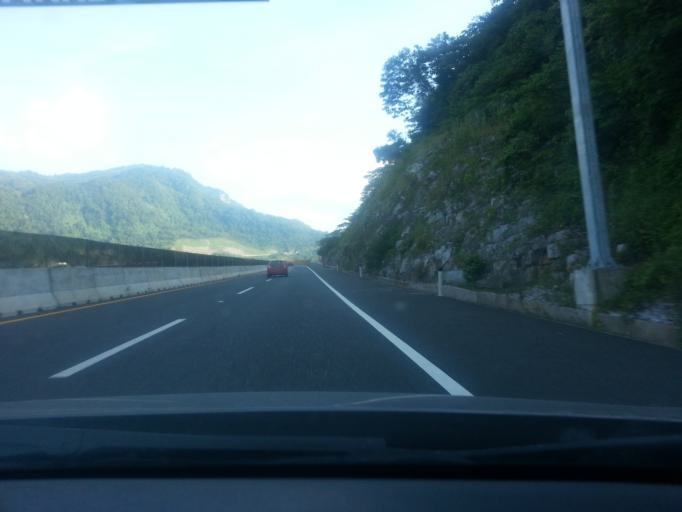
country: MX
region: Puebla
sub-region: Xicotepec
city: San Lorenzo
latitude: 20.3471
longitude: -97.9618
